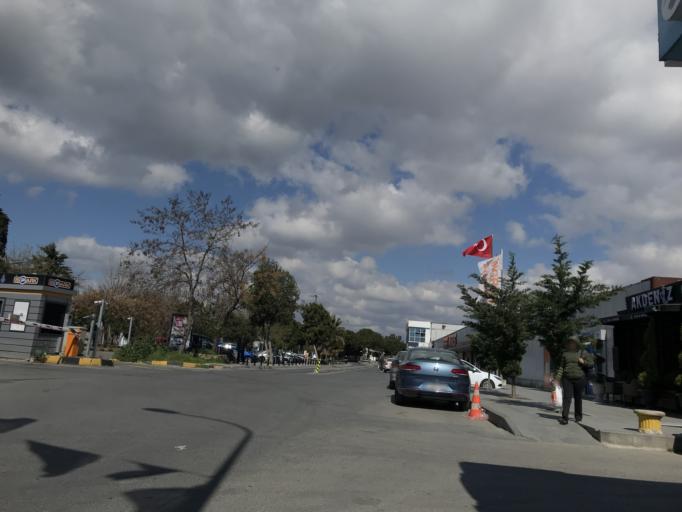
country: TR
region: Istanbul
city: Maltepe
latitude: 40.9253
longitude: 29.1249
